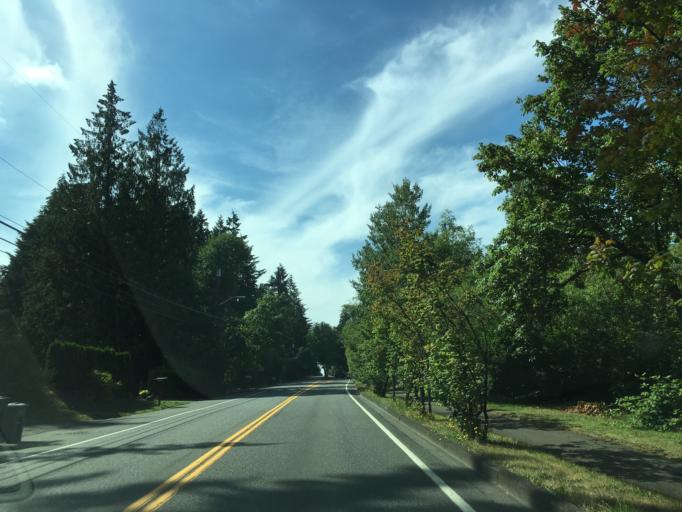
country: US
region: Washington
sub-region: King County
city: Lake Forest Park
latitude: 47.7641
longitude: -122.2938
